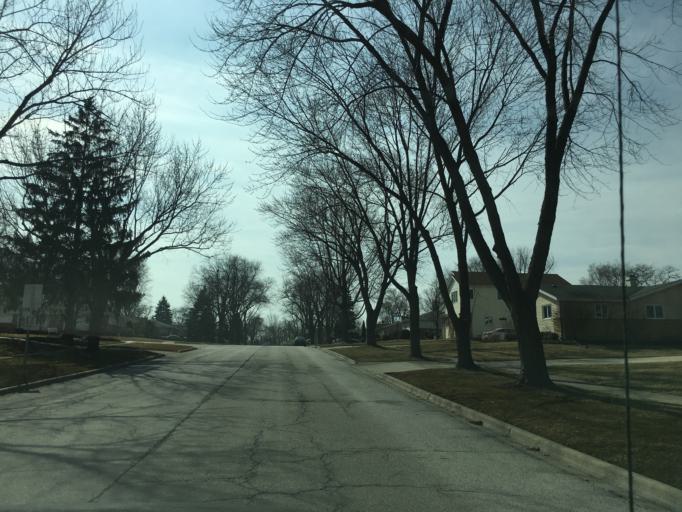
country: US
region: Illinois
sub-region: Cook County
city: Schaumburg
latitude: 42.0345
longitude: -88.0955
